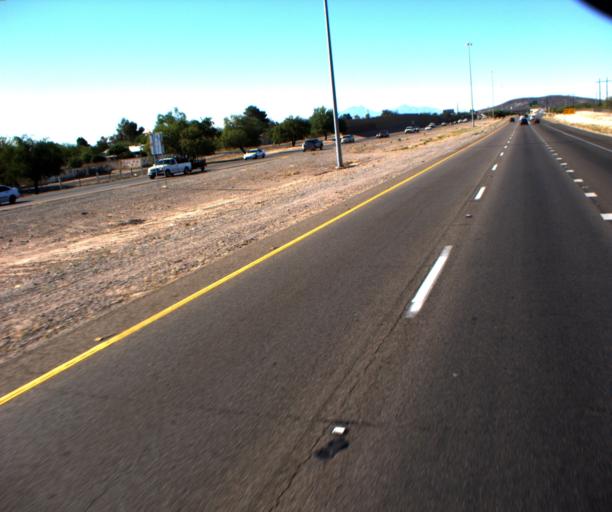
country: US
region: Arizona
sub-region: Pima County
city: Drexel Heights
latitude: 32.1443
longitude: -110.9868
